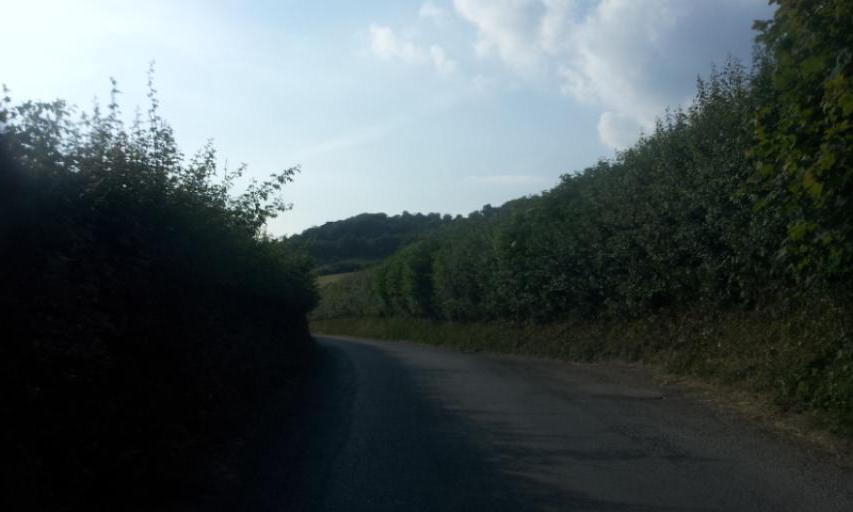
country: GB
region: England
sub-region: Kent
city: Boxley
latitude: 51.2933
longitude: 0.5828
